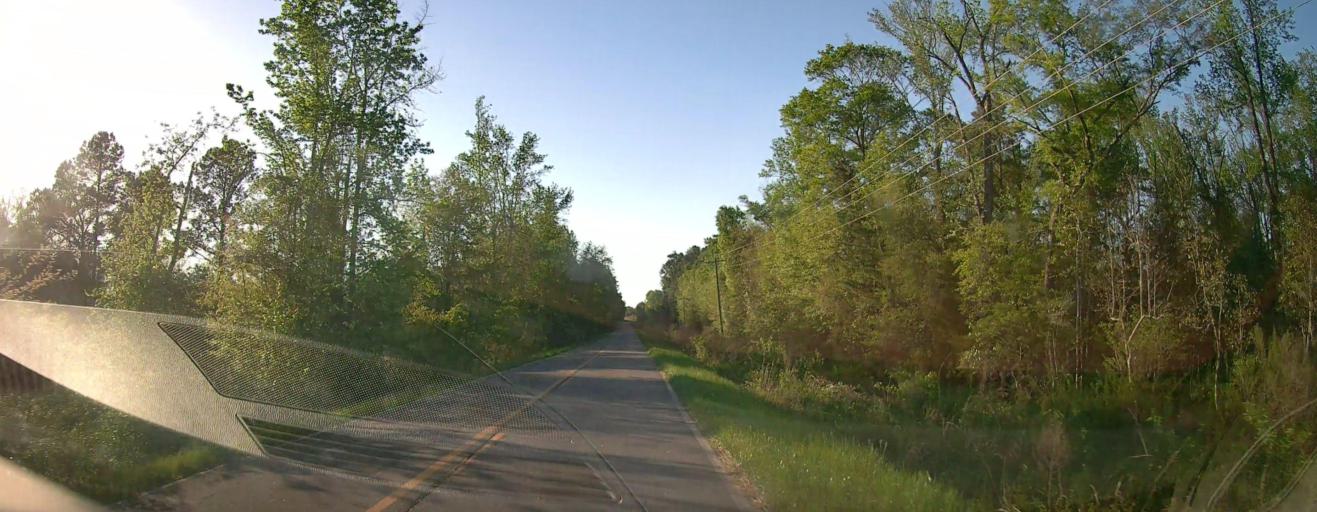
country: US
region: Georgia
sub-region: Macon County
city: Oglethorpe
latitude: 32.2744
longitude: -84.0868
